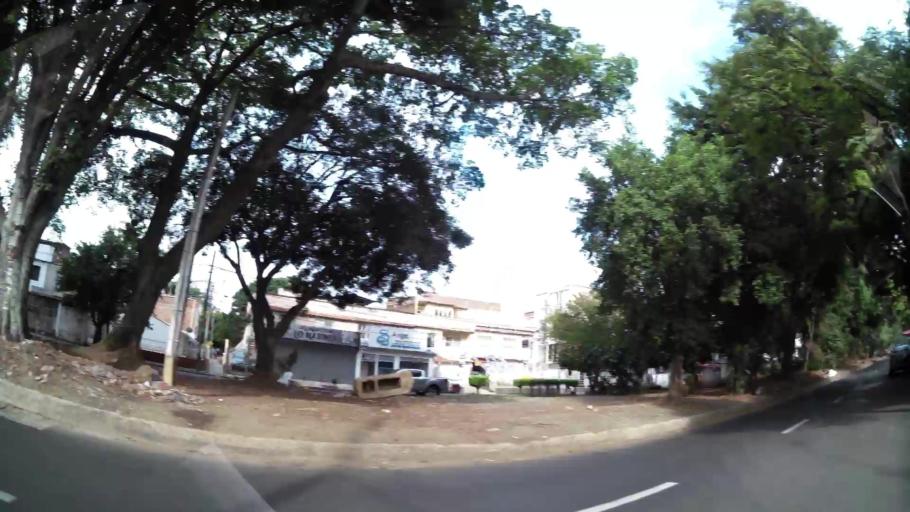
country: CO
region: Valle del Cauca
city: Cali
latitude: 3.4731
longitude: -76.4928
